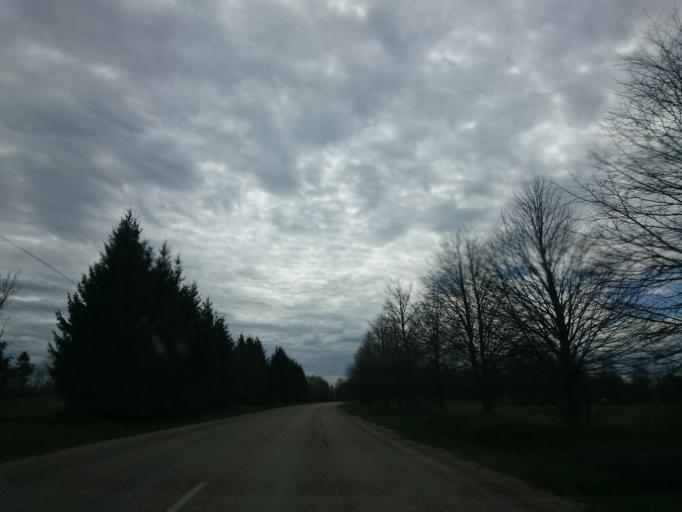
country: LV
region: Aizpute
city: Aizpute
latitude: 56.7404
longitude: 21.6089
